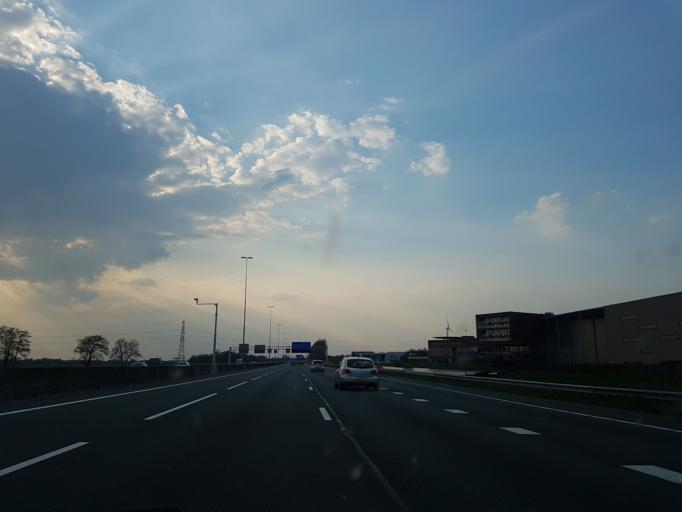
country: NL
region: Gelderland
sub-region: Gemeente Ede
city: Ede
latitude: 52.0200
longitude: 5.6278
